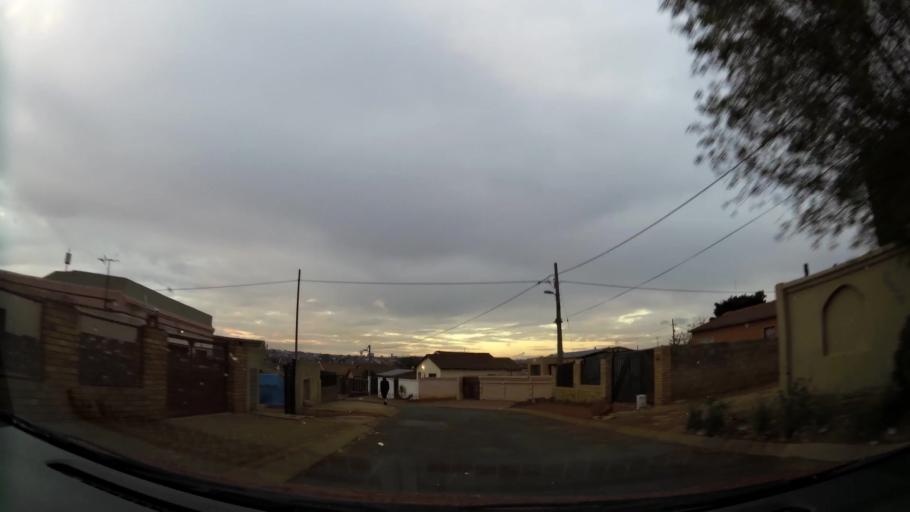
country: ZA
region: Gauteng
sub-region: City of Johannesburg Metropolitan Municipality
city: Roodepoort
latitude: -26.1735
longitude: 27.7899
